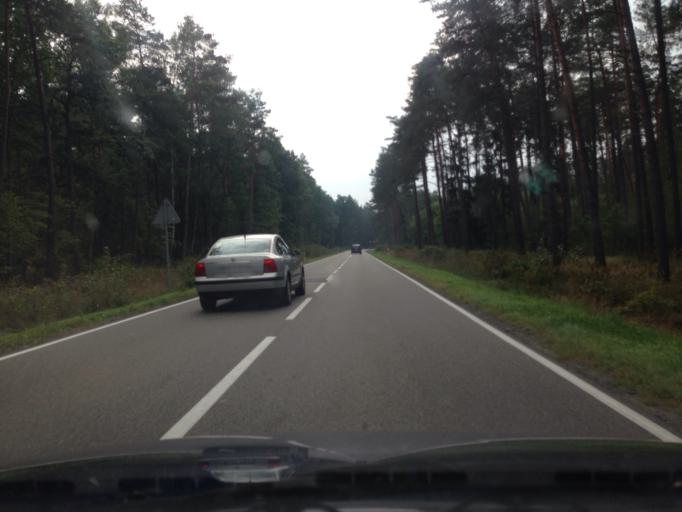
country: PL
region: Pomeranian Voivodeship
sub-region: Powiat kwidzynski
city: Ryjewo
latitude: 53.8321
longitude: 18.9909
